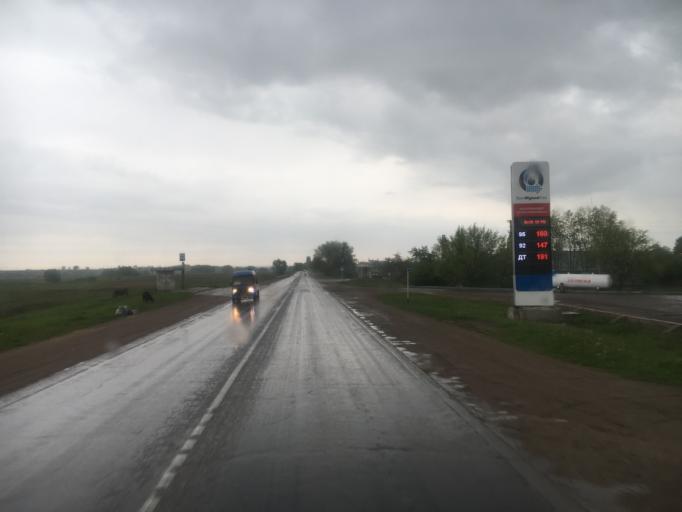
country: KZ
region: Almaty Oblysy
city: Burunday
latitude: 43.2900
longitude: 76.6734
